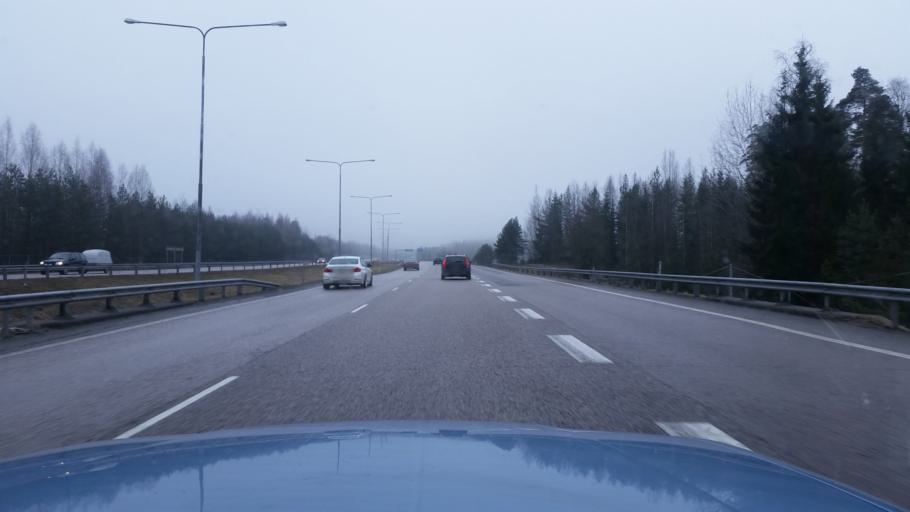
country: FI
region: Uusimaa
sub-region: Helsinki
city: Hyvinge
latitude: 60.5624
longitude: 24.8223
